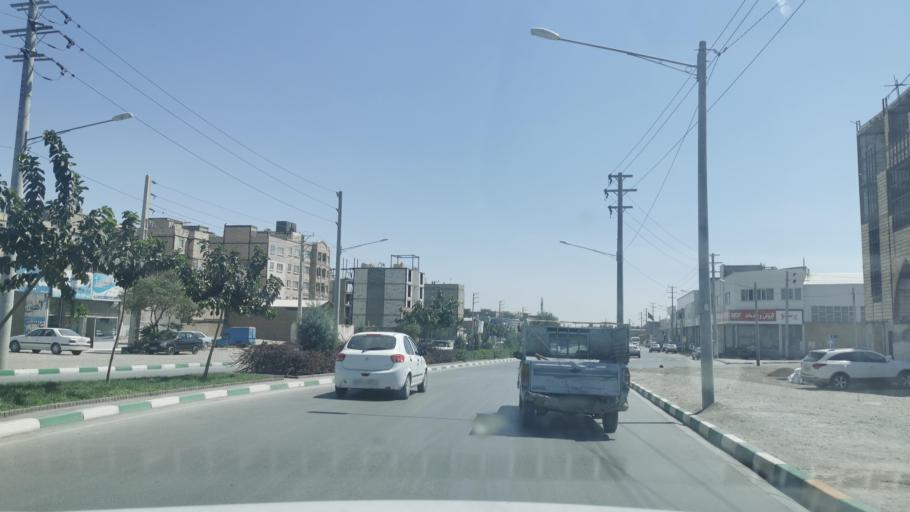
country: IR
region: Razavi Khorasan
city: Mashhad
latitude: 36.3528
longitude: 59.5718
